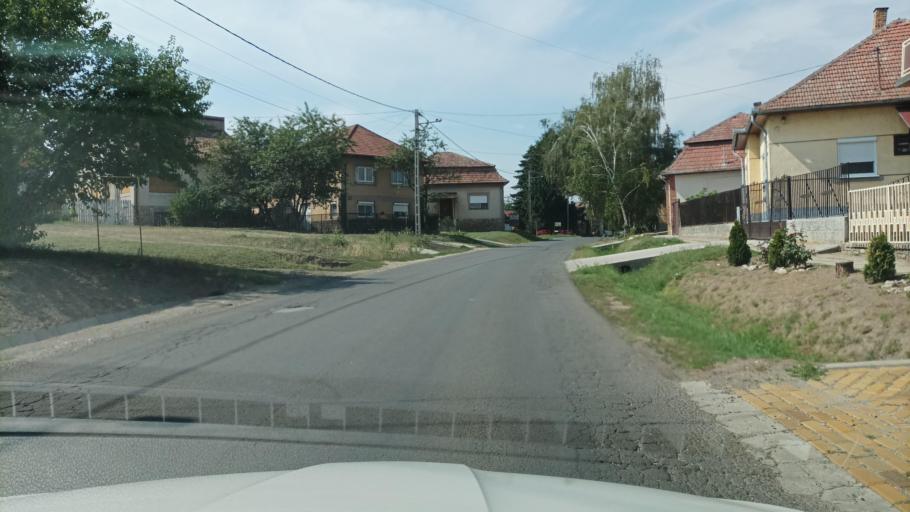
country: HU
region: Pest
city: Galgaheviz
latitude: 47.6223
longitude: 19.5502
